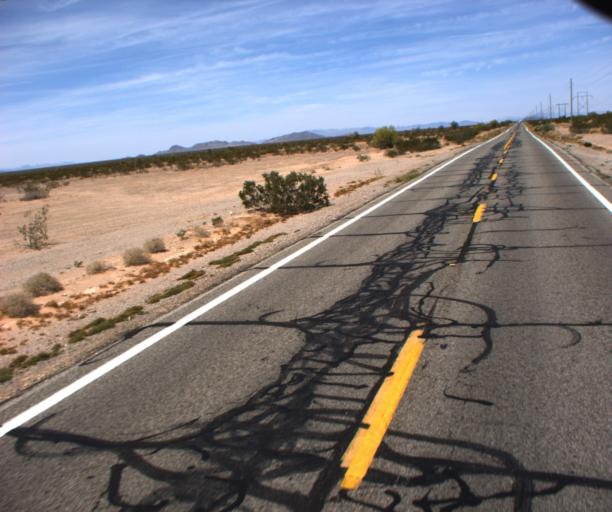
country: US
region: Arizona
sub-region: La Paz County
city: Quartzsite
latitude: 33.8319
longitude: -114.2170
